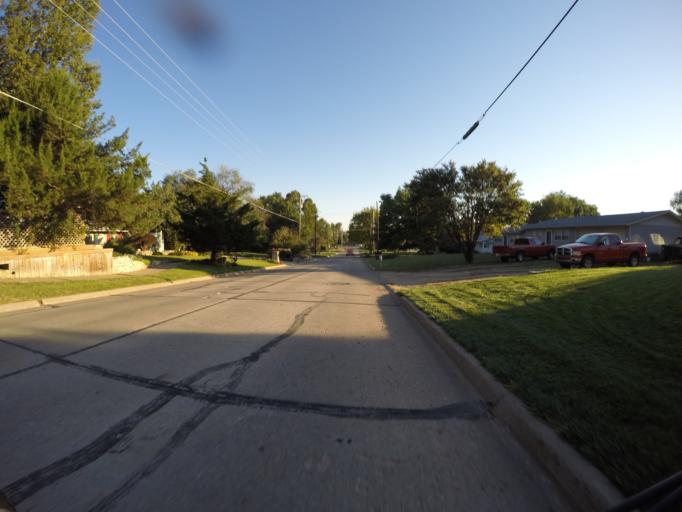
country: US
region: Kansas
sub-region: Riley County
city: Manhattan
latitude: 39.1911
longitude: -96.6260
